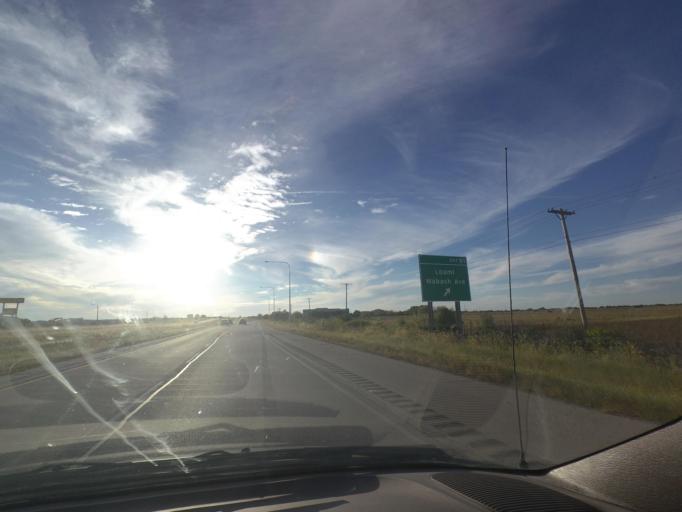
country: US
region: Illinois
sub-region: Sangamon County
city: Jerome
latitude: 39.7522
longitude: -89.7415
